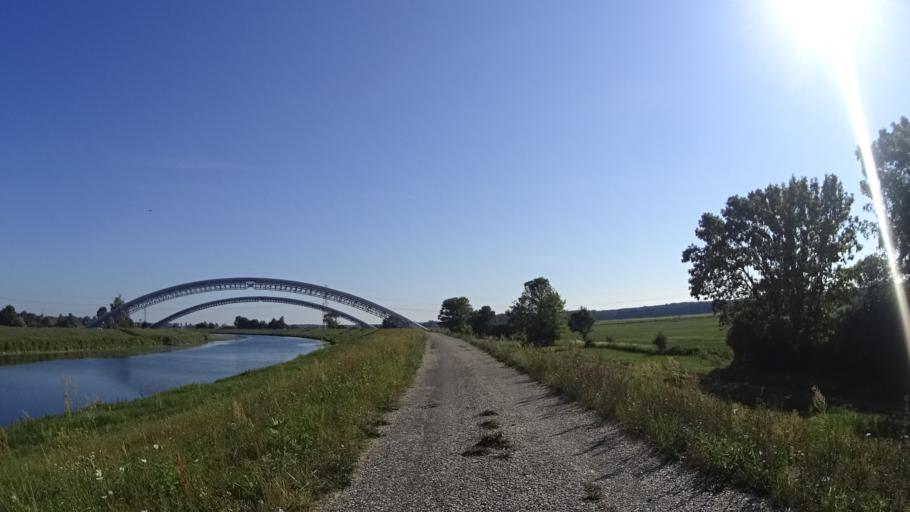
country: CZ
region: South Moravian
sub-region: Okres Breclav
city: Lanzhot
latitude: 48.7150
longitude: 17.0091
